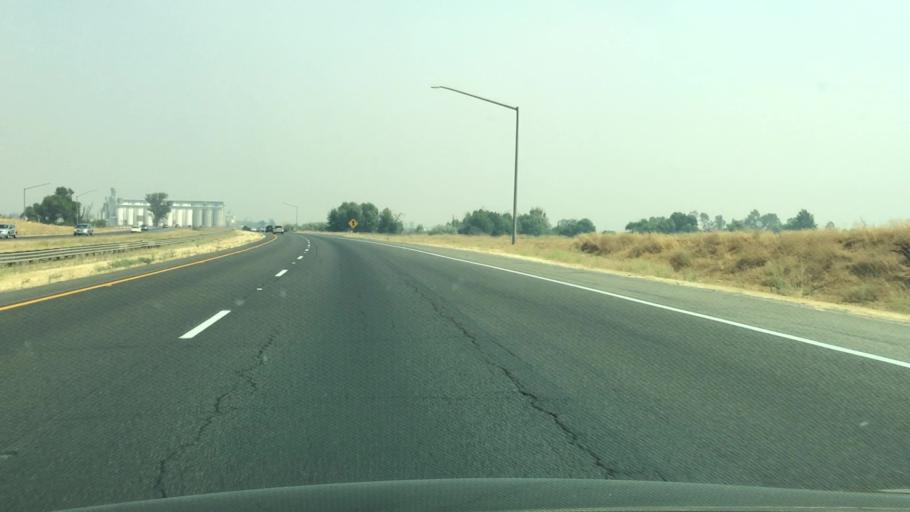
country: US
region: California
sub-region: Madera County
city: Madera Acres
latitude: 37.0179
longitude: -120.1286
